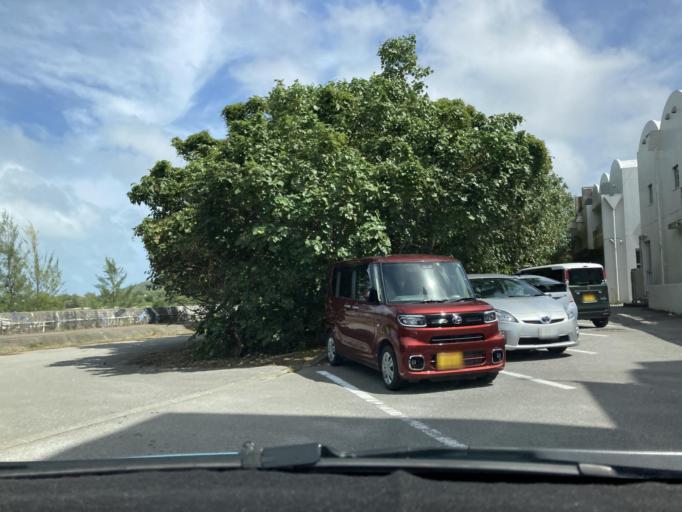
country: JP
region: Okinawa
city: Ginowan
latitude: 26.1704
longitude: 127.7875
